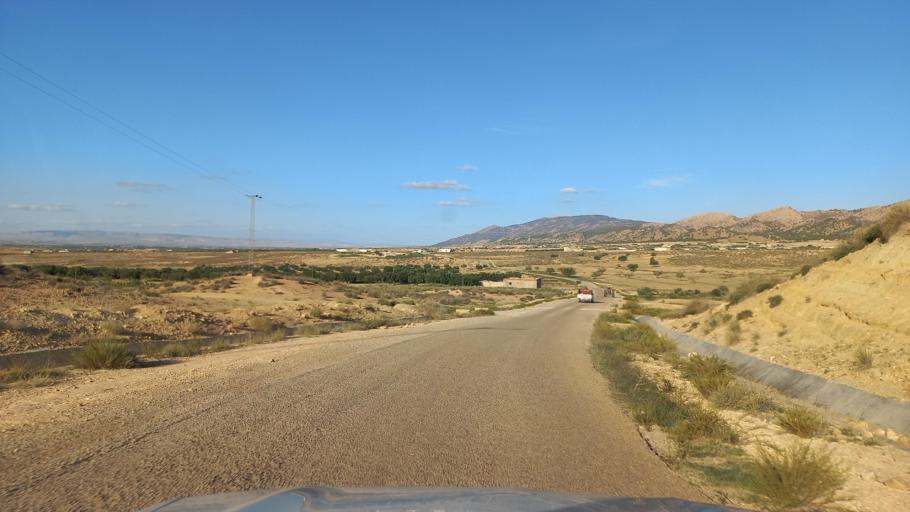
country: TN
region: Al Qasrayn
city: Sbiba
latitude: 35.3501
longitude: 9.1319
